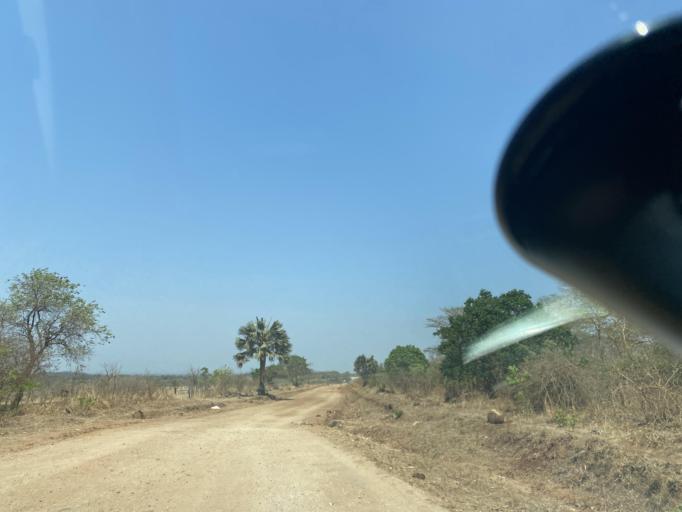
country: ZM
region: Lusaka
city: Lusaka
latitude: -15.5314
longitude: 28.0960
